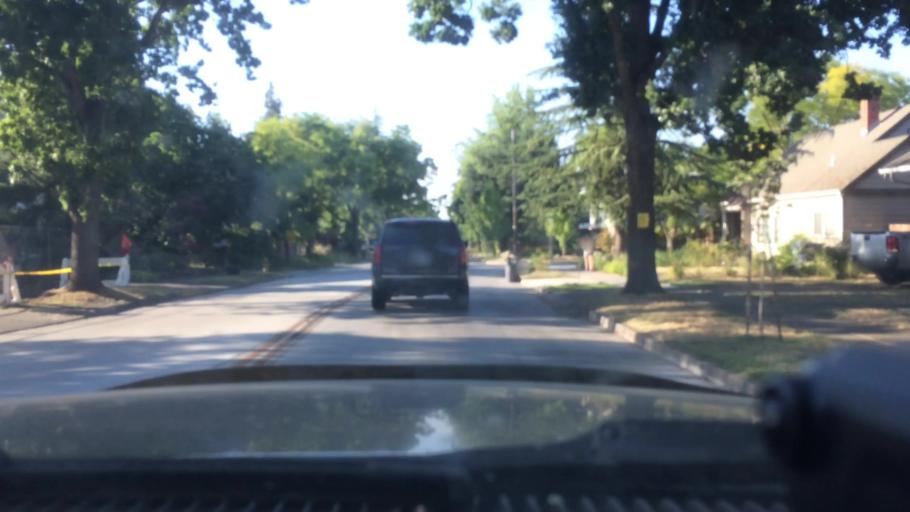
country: US
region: Oregon
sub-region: Lane County
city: Eugene
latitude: 44.0407
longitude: -123.1013
